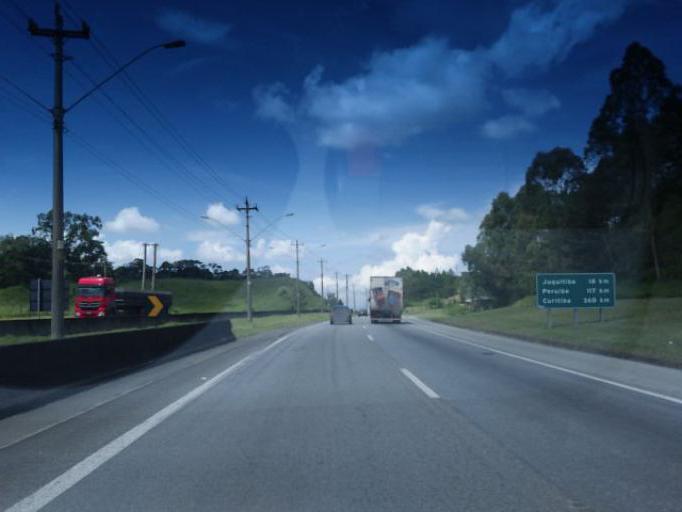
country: BR
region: Sao Paulo
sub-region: Sao Lourenco Da Serra
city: Sao Lourenco da Serra
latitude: -23.8659
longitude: -46.9506
